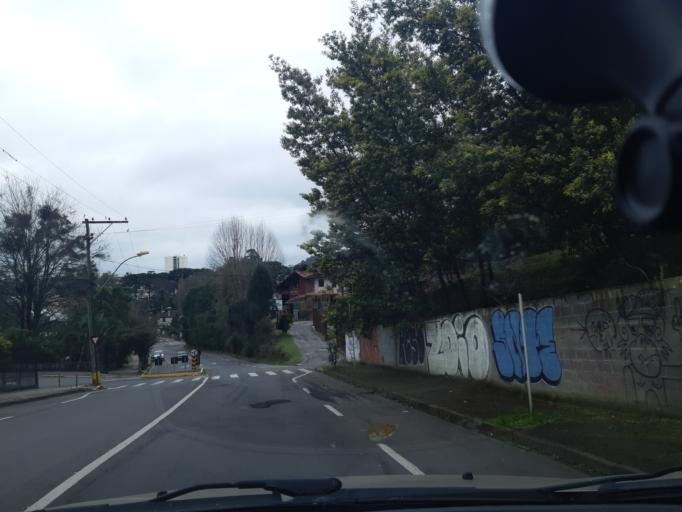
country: BR
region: Rio Grande do Sul
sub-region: Caxias Do Sul
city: Caxias do Sul
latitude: -29.1580
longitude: -51.1985
